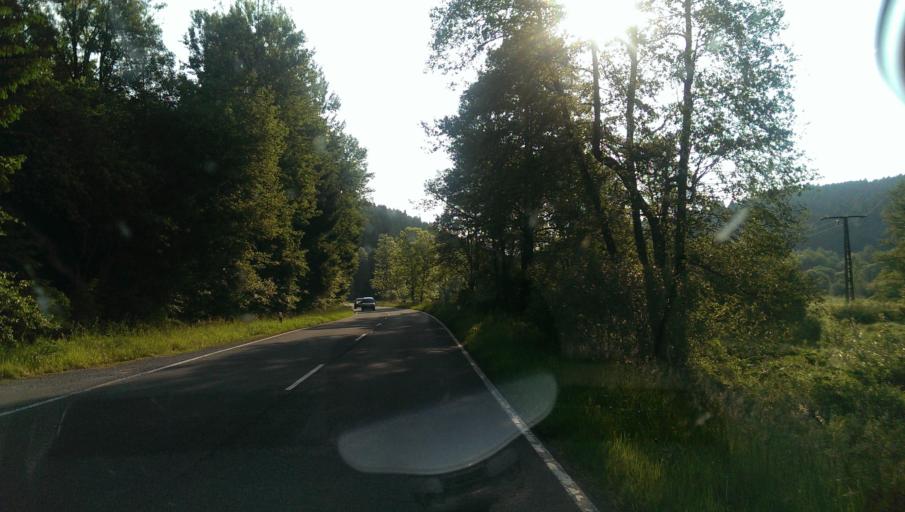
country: DE
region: Thuringia
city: Dillstadt
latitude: 50.5935
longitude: 10.5527
